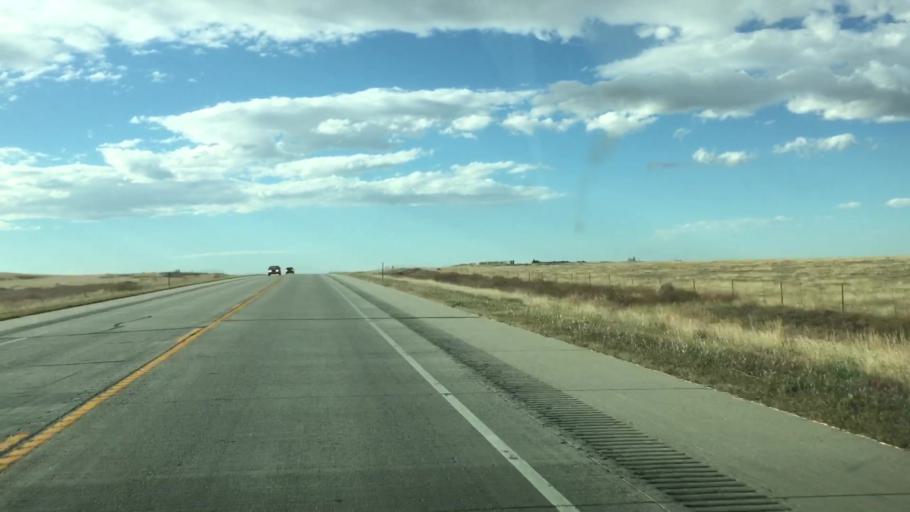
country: US
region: Colorado
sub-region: Lincoln County
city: Hugo
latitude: 39.1742
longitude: -103.5368
